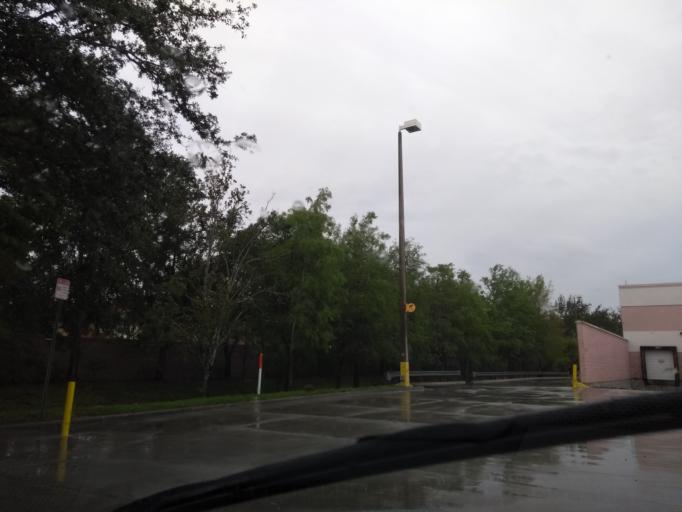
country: US
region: Florida
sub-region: Collier County
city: Pine Ridge
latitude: 26.2079
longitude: -81.7661
